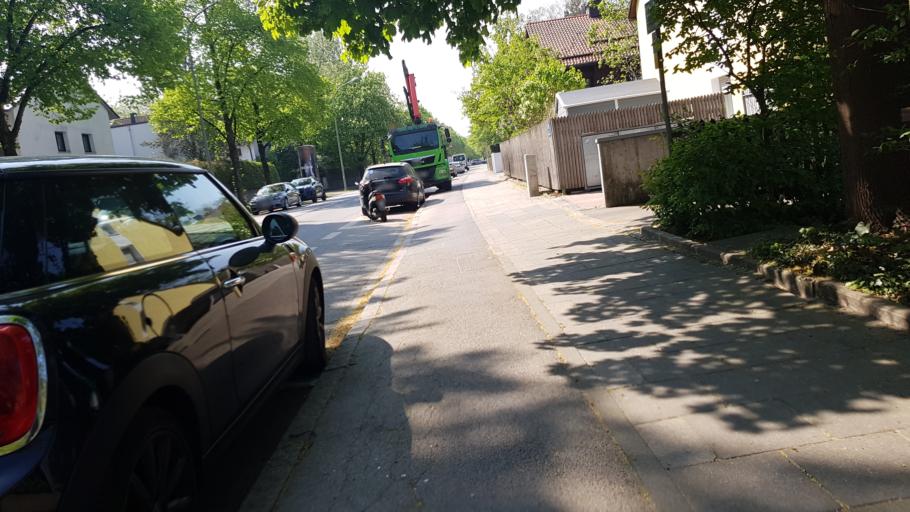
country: DE
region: Bavaria
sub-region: Upper Bavaria
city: Bogenhausen
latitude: 48.1494
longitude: 11.6285
